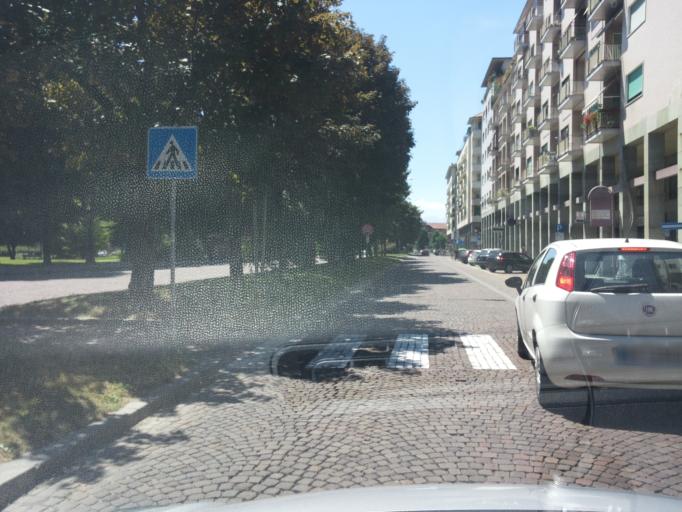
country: IT
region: Piedmont
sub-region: Provincia di Biella
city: Biella
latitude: 45.5617
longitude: 8.0524
